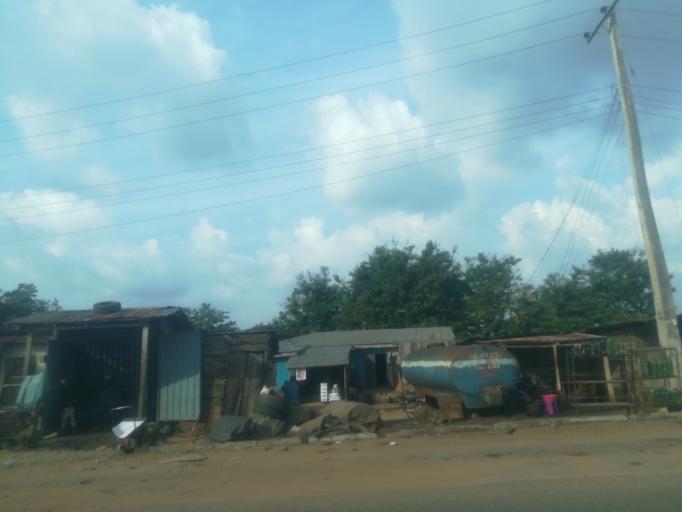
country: NG
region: Oyo
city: Ibadan
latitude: 7.3907
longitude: 3.8167
